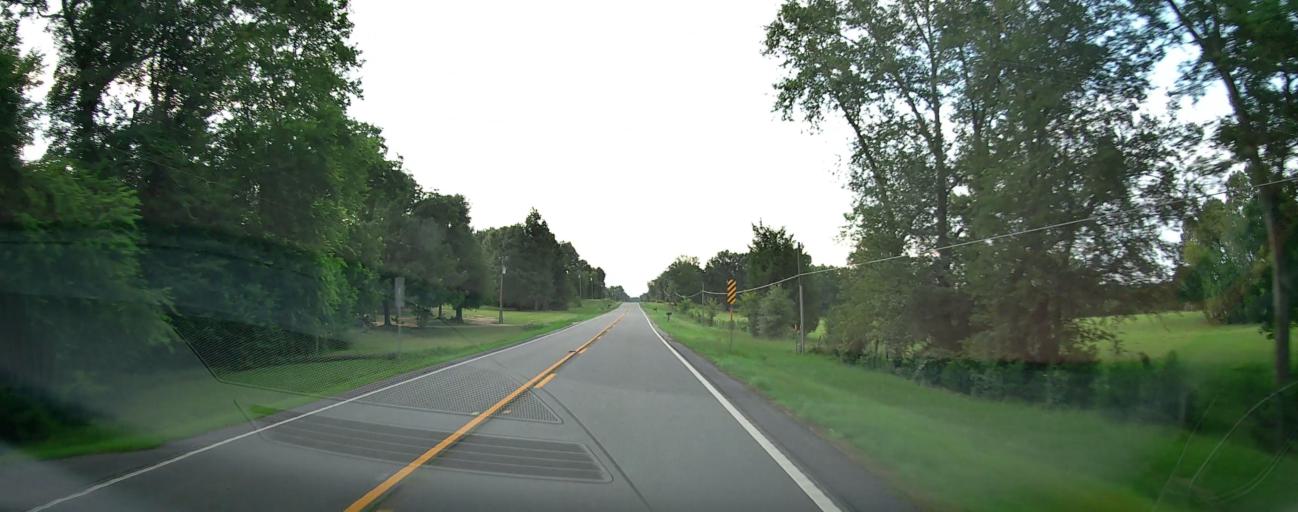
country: US
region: Georgia
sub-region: Taylor County
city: Reynolds
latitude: 32.6010
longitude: -84.0943
